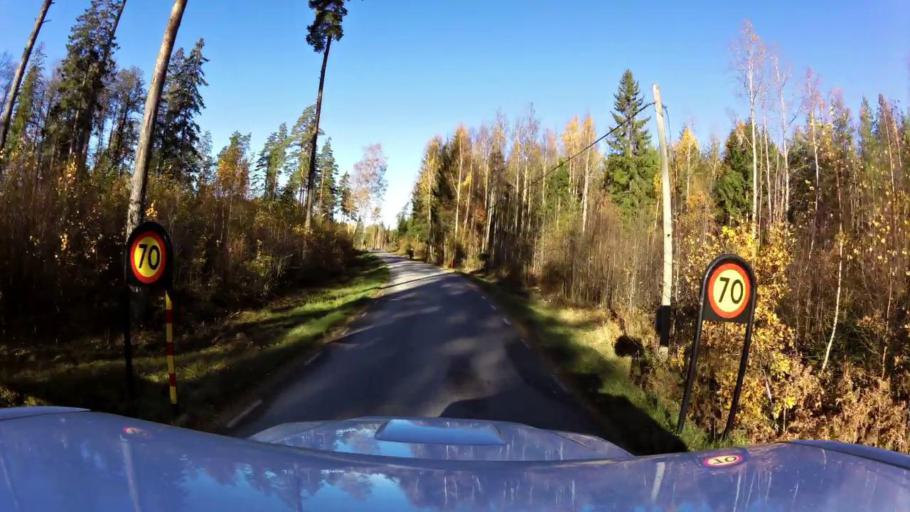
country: SE
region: OEstergoetland
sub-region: Linkopings Kommun
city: Ljungsbro
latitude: 58.5238
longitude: 15.4892
